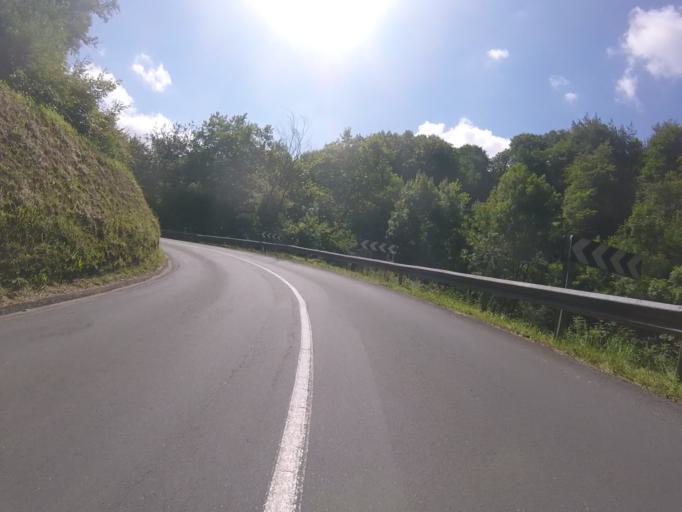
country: ES
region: Basque Country
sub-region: Provincia de Guipuzcoa
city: Errezil
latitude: 43.1741
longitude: -2.2160
